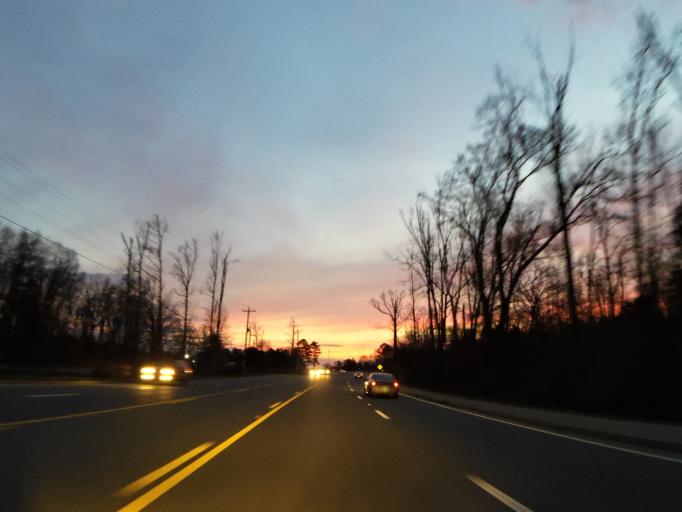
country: US
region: Tennessee
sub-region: Polk County
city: Benton
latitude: 35.1452
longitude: -84.7073
